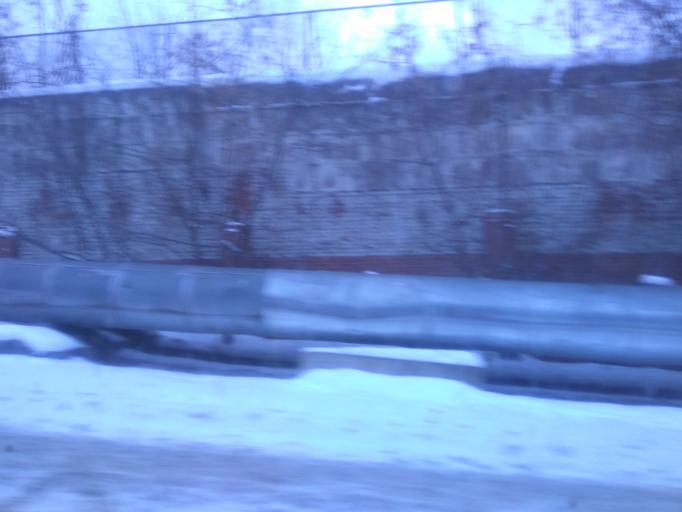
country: RU
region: Moscow
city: Taganskiy
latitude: 55.7283
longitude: 37.6938
